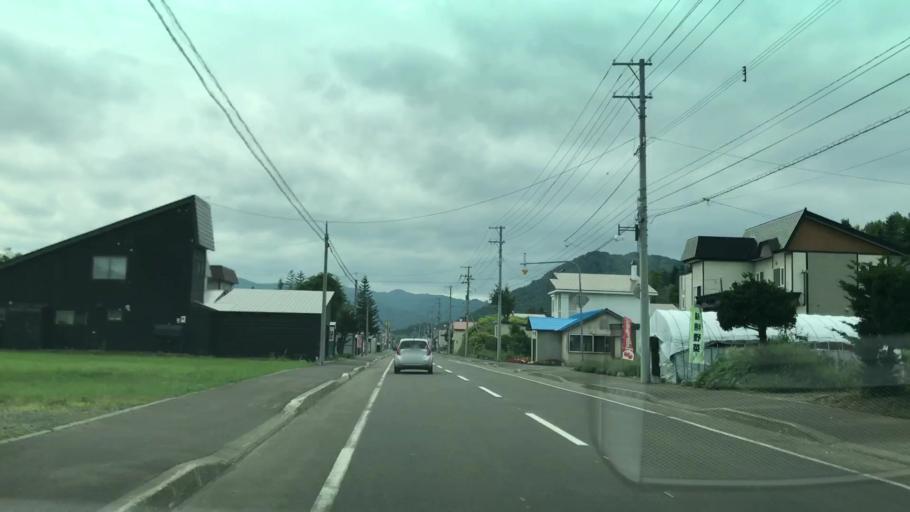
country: JP
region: Hokkaido
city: Yoichi
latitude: 43.0880
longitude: 140.8154
